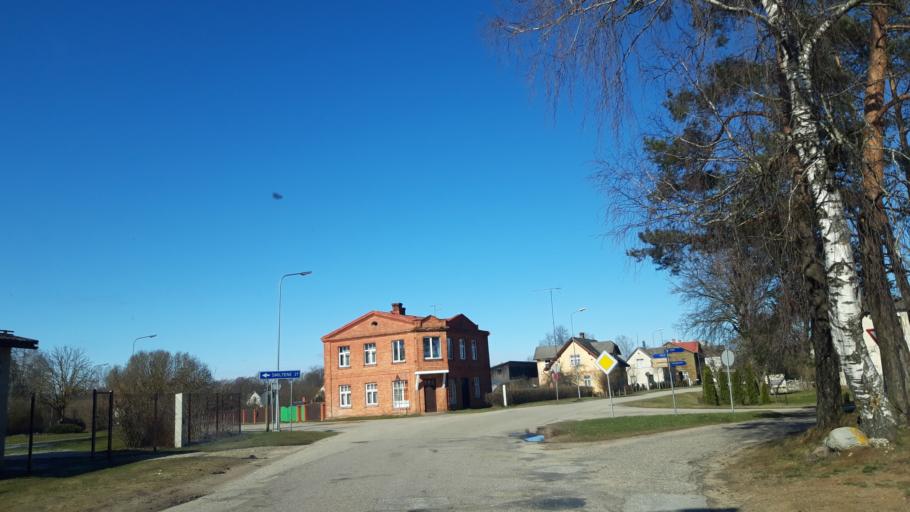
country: LV
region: Strenci
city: Strenci
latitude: 57.6236
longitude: 25.6944
